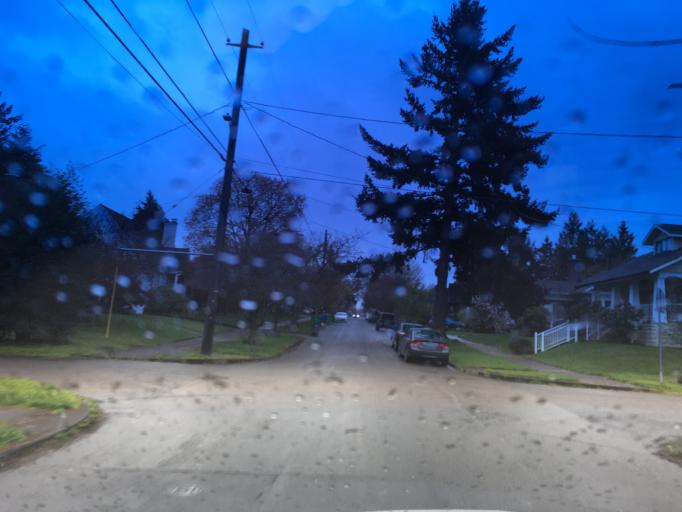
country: US
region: Oregon
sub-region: Multnomah County
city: Lents
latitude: 45.5527
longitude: -122.5932
